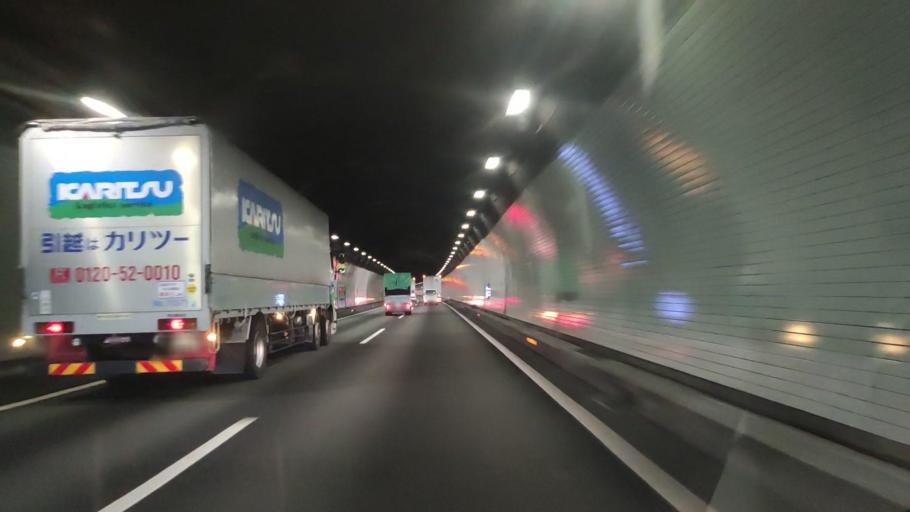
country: JP
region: Tokyo
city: Fussa
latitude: 35.7563
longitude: 139.2846
